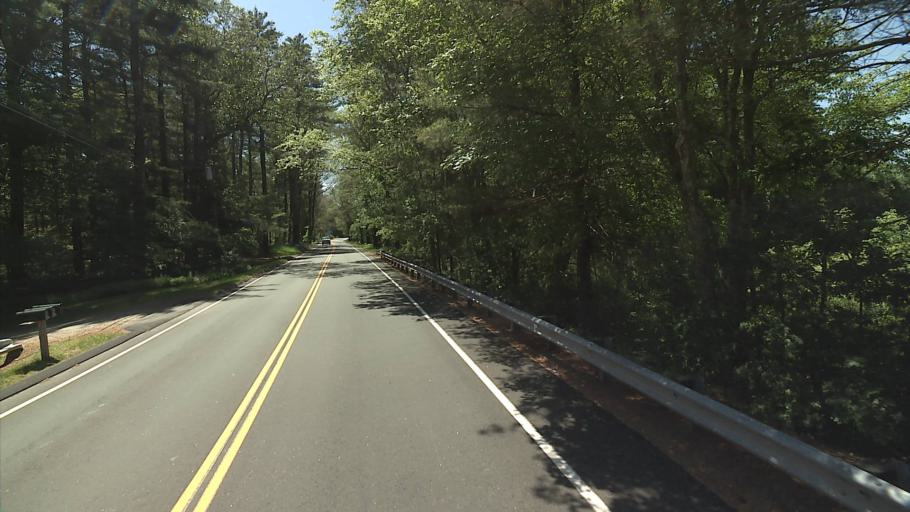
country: US
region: Connecticut
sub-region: Windham County
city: Plainfield
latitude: 41.5840
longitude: -71.8553
